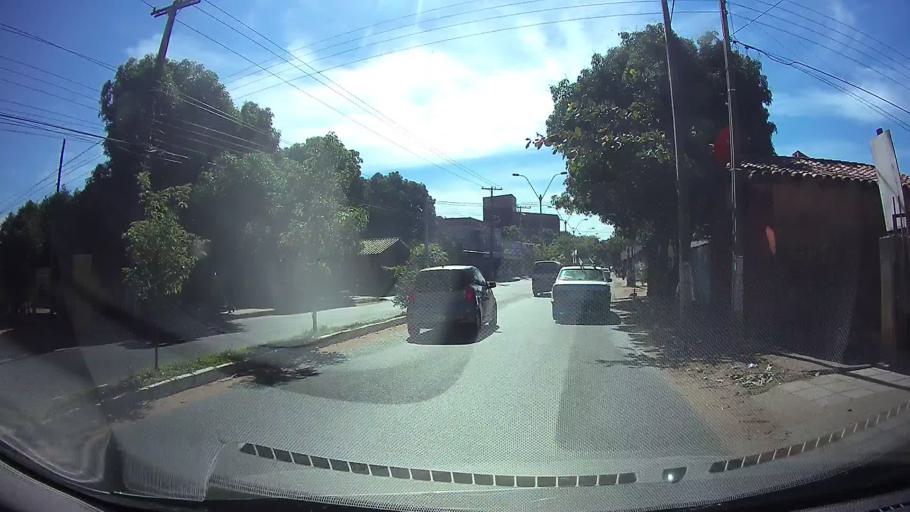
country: PY
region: Central
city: Villa Elisa
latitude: -25.3658
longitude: -57.5783
